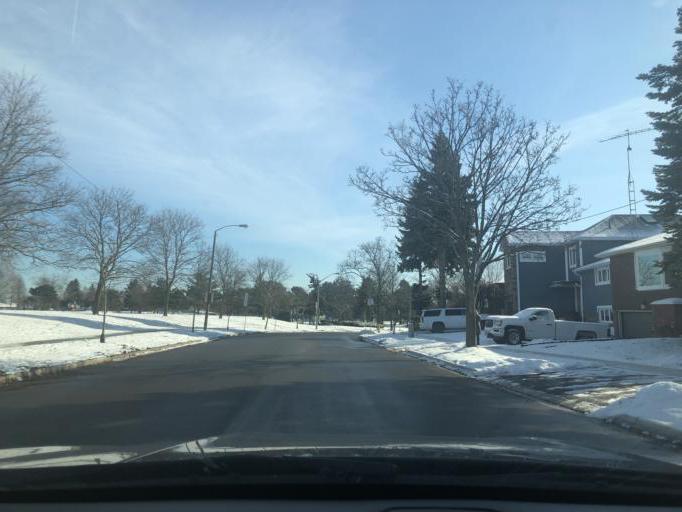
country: CA
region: Ontario
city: Scarborough
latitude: 43.7815
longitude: -79.1422
